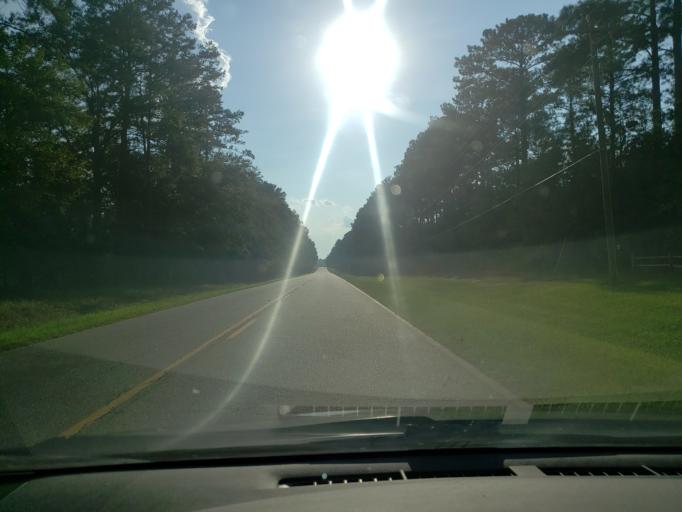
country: US
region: Georgia
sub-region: Terrell County
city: Dawson
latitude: 31.5774
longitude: -84.3777
